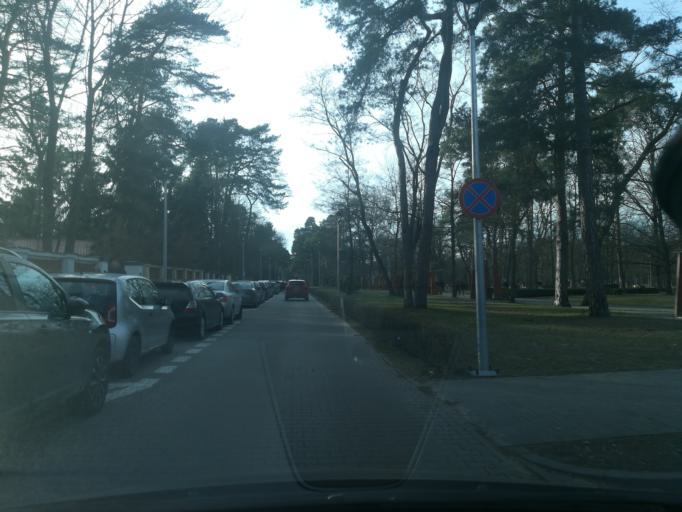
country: PL
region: Masovian Voivodeship
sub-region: Powiat piaseczynski
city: Konstancin-Jeziorna
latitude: 52.0842
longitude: 21.1165
